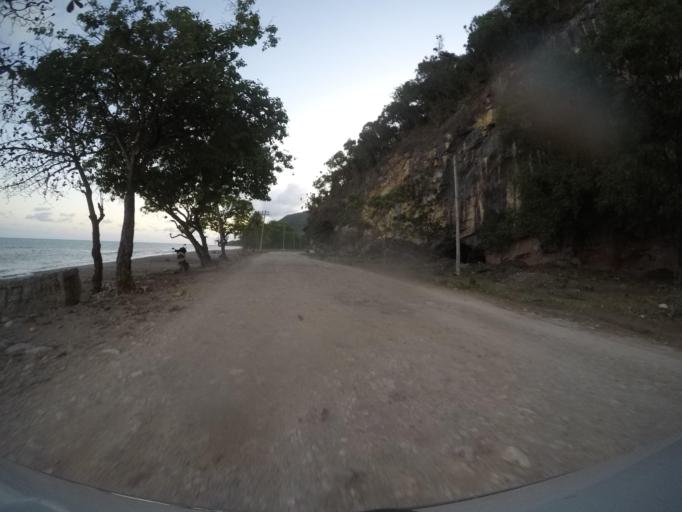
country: TL
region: Viqueque
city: Viqueque
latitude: -8.7866
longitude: 126.6335
